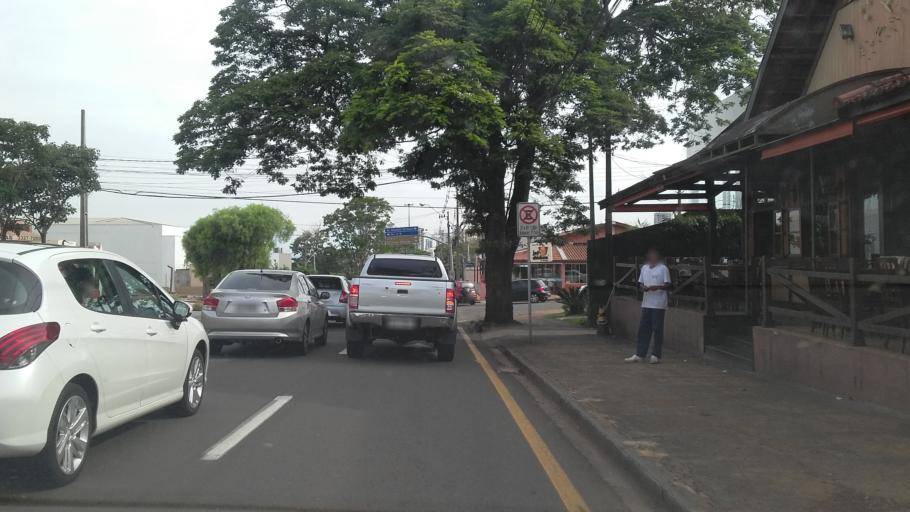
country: BR
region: Parana
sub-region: Londrina
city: Londrina
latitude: -23.3127
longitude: -51.1776
